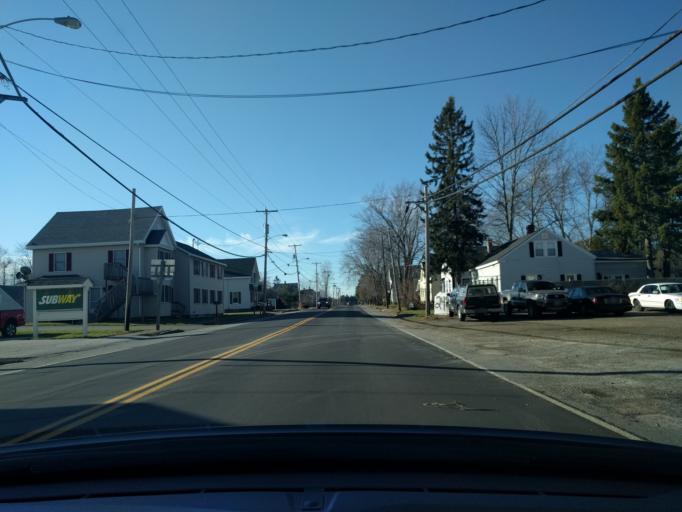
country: US
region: Maine
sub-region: Penobscot County
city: Hampden
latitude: 44.7448
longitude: -68.8383
